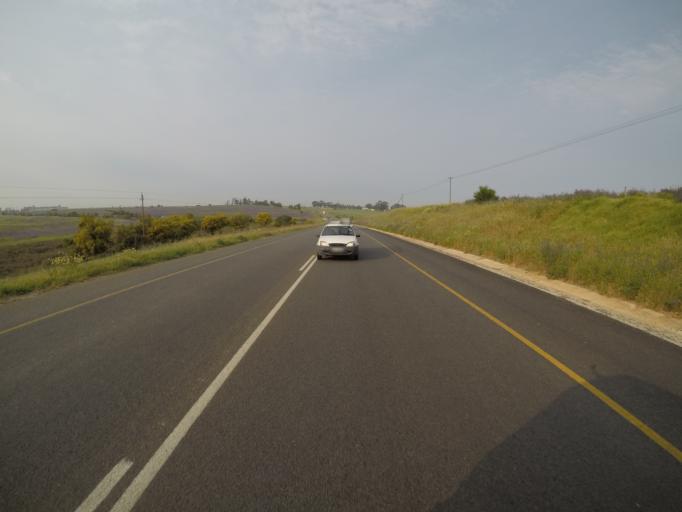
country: ZA
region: Western Cape
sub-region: West Coast District Municipality
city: Malmesbury
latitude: -33.5844
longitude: 18.7330
